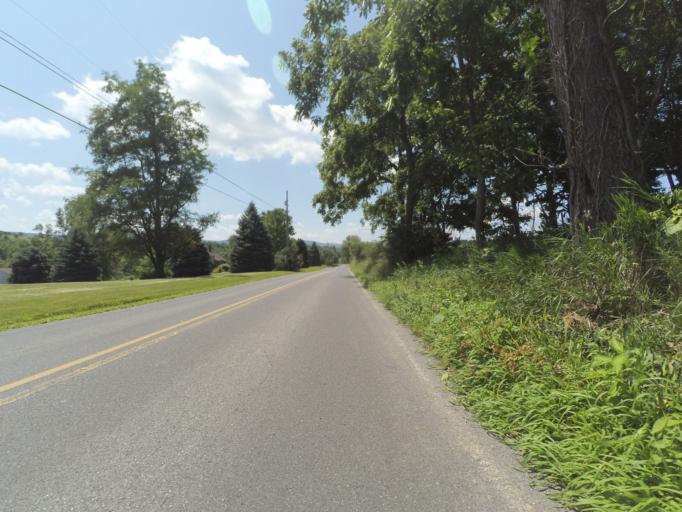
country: US
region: Pennsylvania
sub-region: Centre County
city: Pleasant Gap
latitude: 40.8110
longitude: -77.7404
